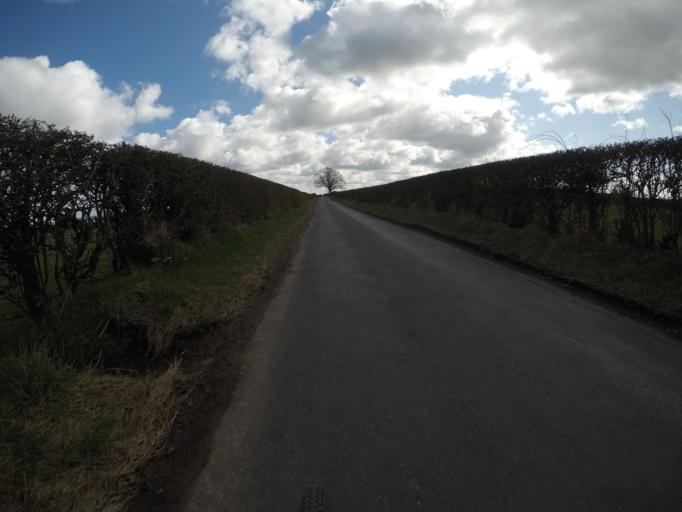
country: GB
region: Scotland
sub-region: South Ayrshire
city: Dundonald
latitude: 55.5895
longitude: -4.5907
